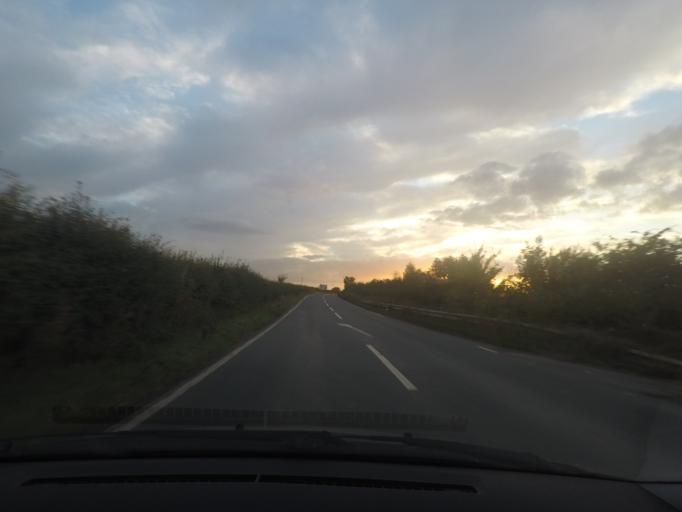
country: GB
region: England
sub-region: North Lincolnshire
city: Croxton
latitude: 53.5852
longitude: -0.3606
